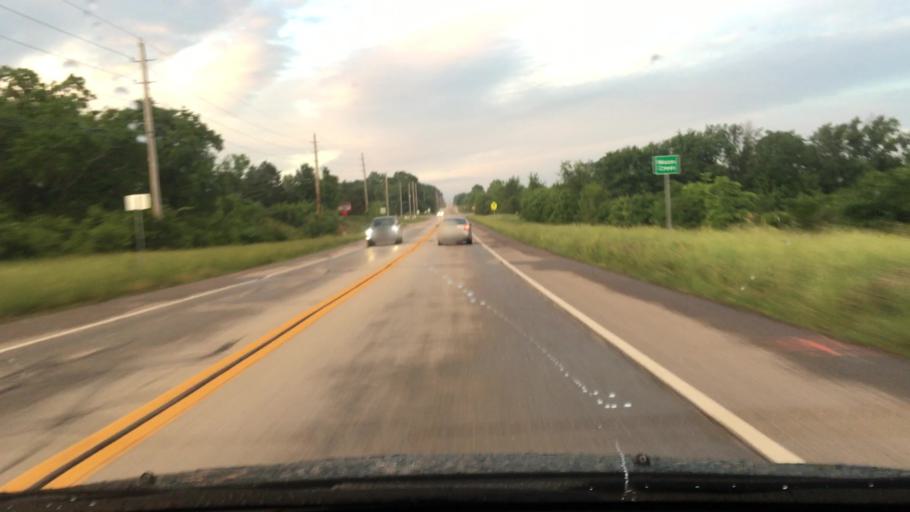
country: US
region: Missouri
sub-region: Jackson County
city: Lees Summit
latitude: 38.8720
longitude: -94.4161
